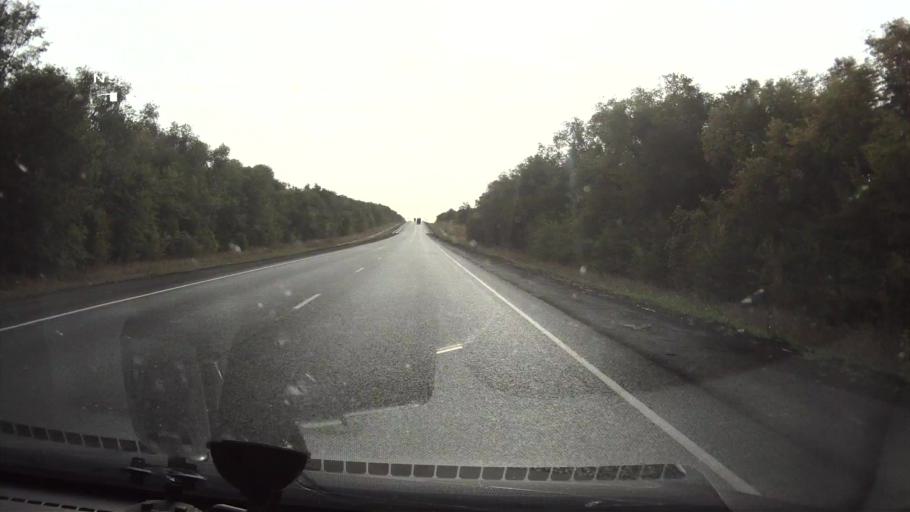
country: RU
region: Saratov
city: Sinodskoye
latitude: 51.9661
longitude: 46.6332
